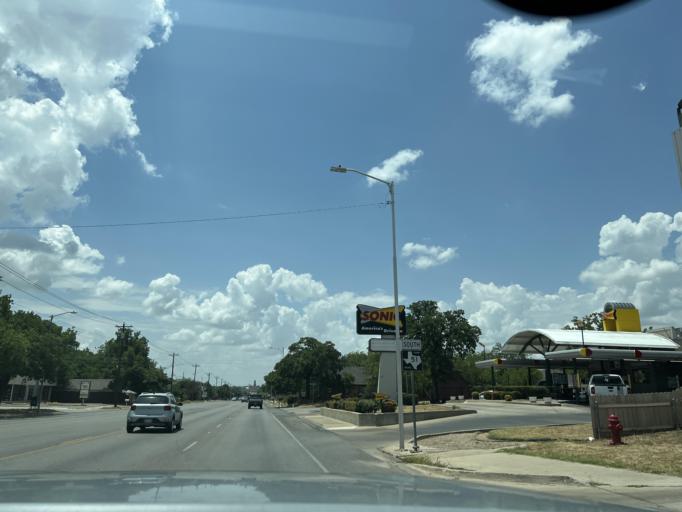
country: US
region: Texas
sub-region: Parker County
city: Weatherford
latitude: 32.7731
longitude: -97.7974
